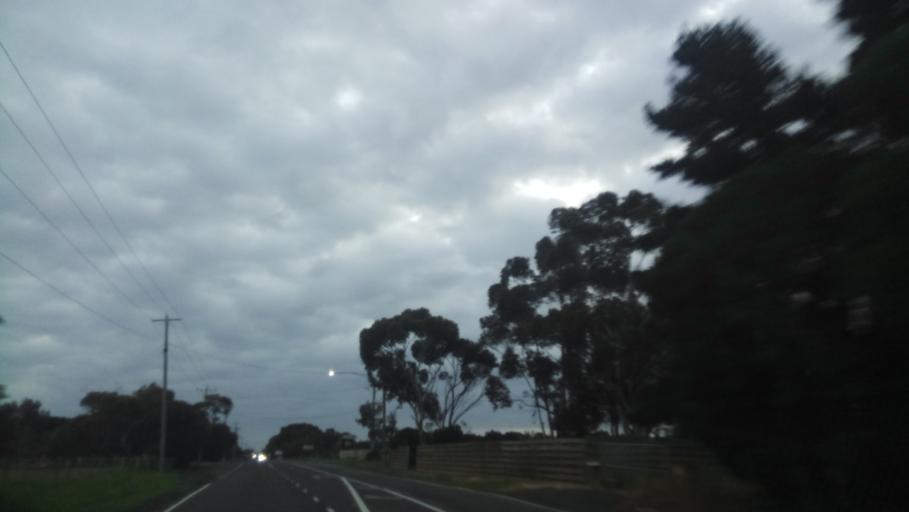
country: AU
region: Victoria
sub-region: Wyndham
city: Point Cook
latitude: -37.9166
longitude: 144.7507
